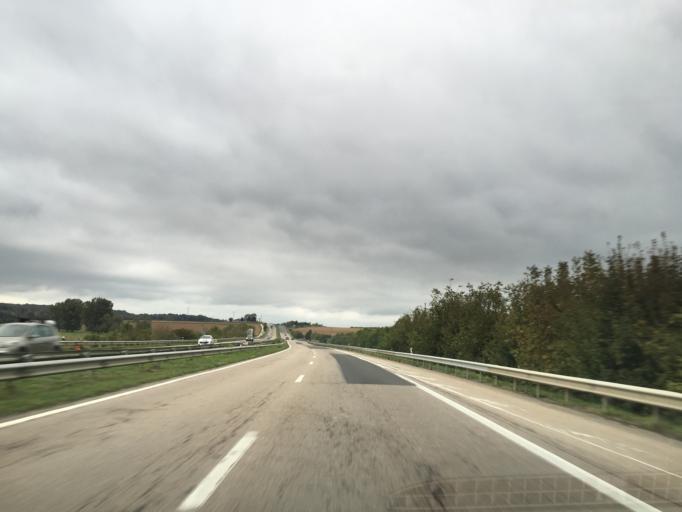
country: FR
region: Lorraine
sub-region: Departement de Meurthe-et-Moselle
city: Foug
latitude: 48.6900
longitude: 5.7000
